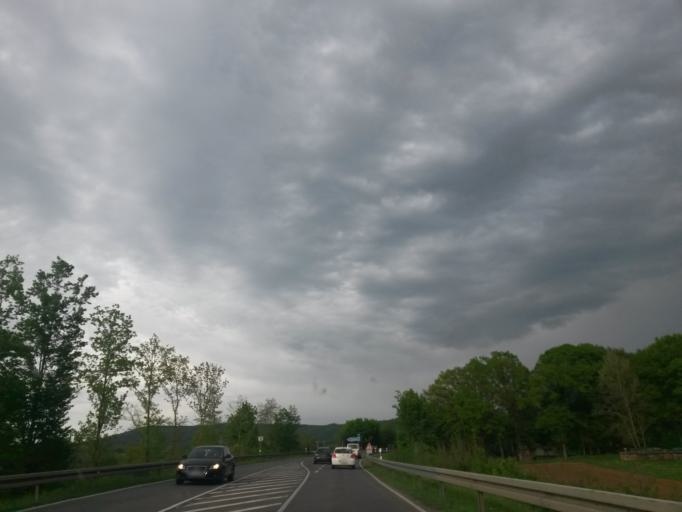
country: DE
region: Bavaria
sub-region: Upper Franconia
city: Hirschaid
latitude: 49.8232
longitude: 11.0054
